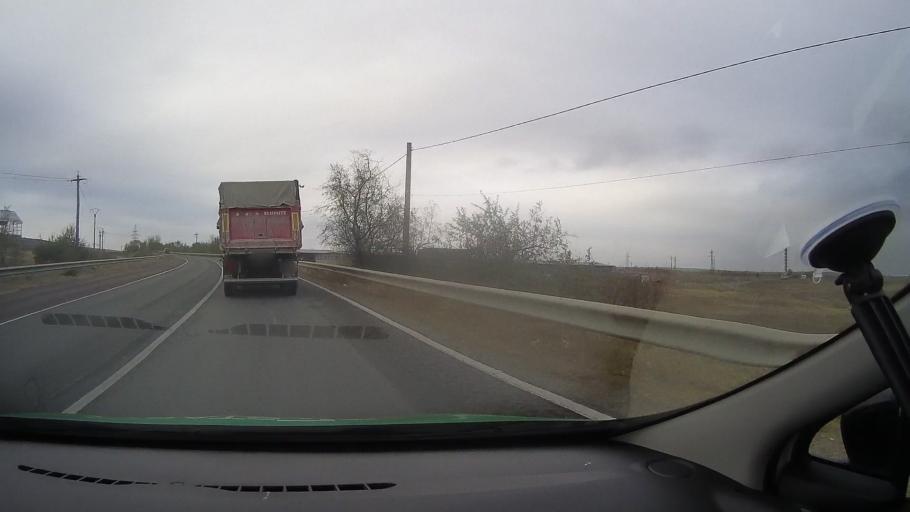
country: RO
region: Constanta
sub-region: Comuna Poarta Alba
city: Poarta Alba
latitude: 44.2133
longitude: 28.3939
